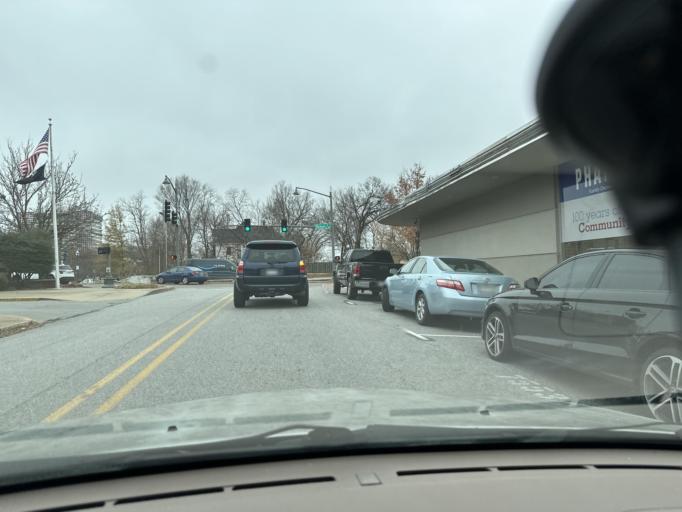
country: US
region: Arkansas
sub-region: Washington County
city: Fayetteville
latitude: 36.0667
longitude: -94.1608
